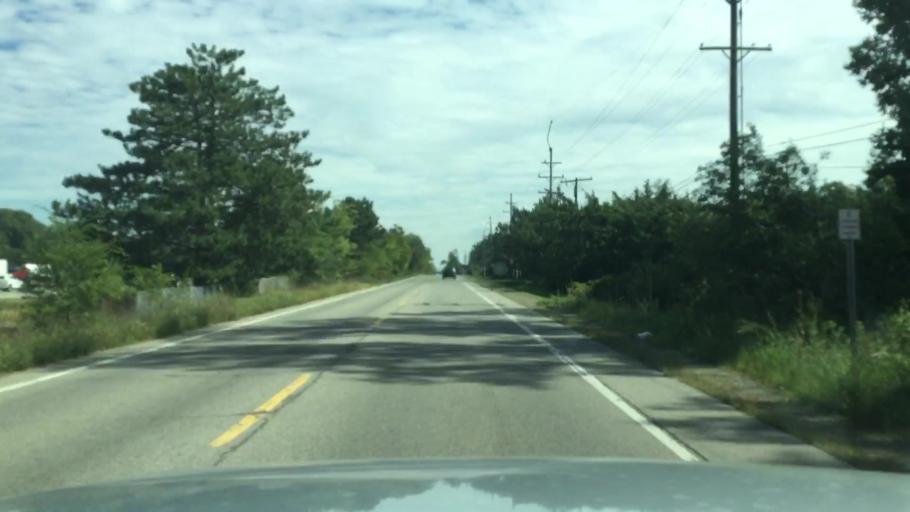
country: US
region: Michigan
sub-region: Wayne County
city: Belleville
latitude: 42.2188
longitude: -83.5018
